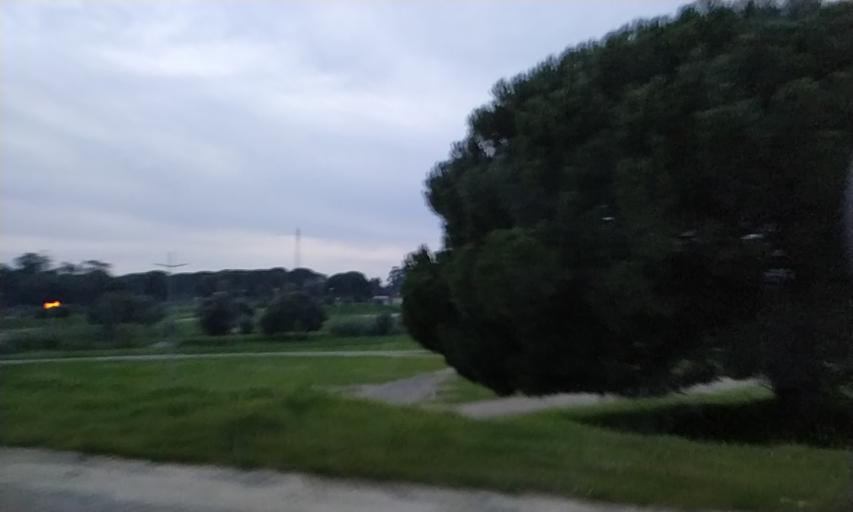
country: PT
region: Setubal
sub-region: Setubal
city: Setubal
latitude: 38.5194
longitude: -8.8497
